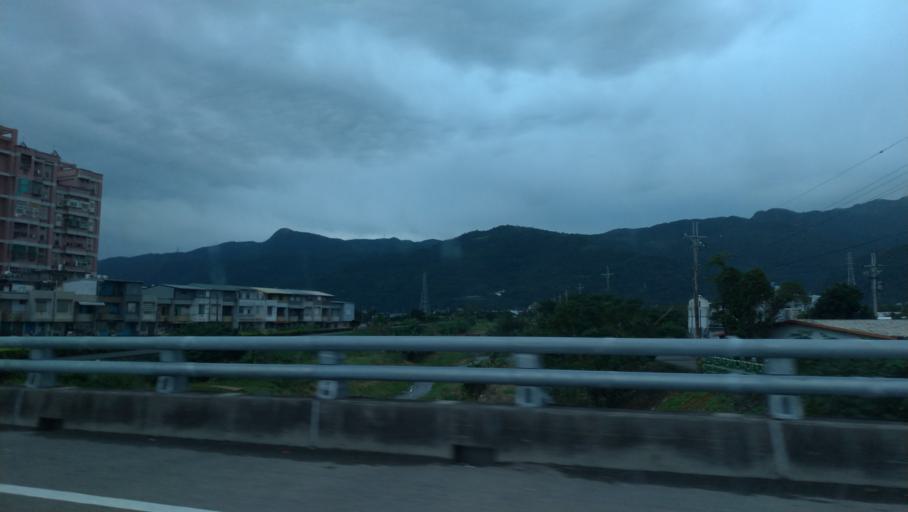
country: TW
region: Taiwan
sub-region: Yilan
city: Yilan
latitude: 24.8487
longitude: 121.8144
